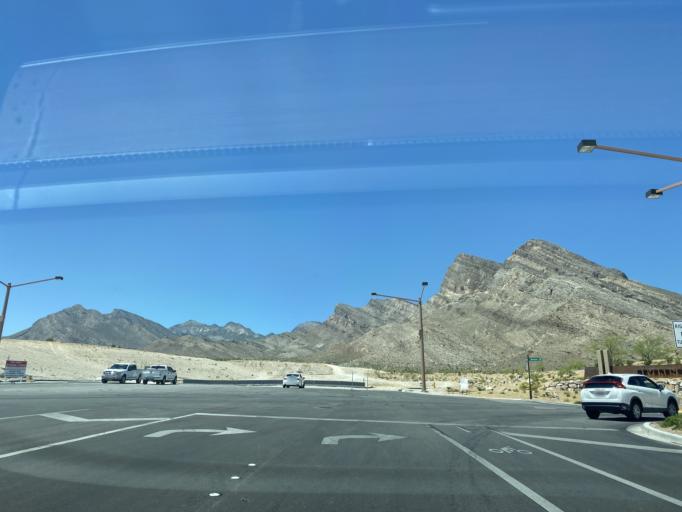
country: US
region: Nevada
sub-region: Clark County
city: Summerlin South
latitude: 36.2069
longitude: -115.3452
